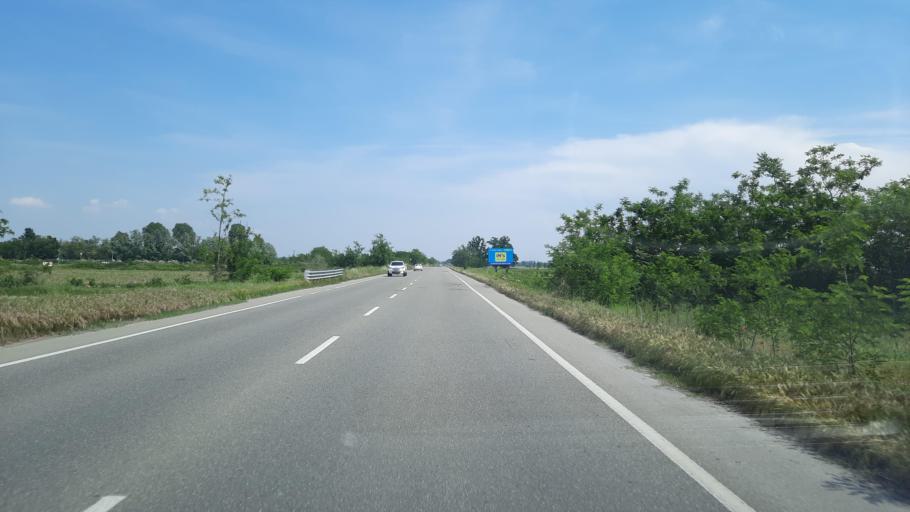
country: IT
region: Lombardy
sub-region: Provincia di Pavia
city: Gambolo
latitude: 45.2284
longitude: 8.8192
